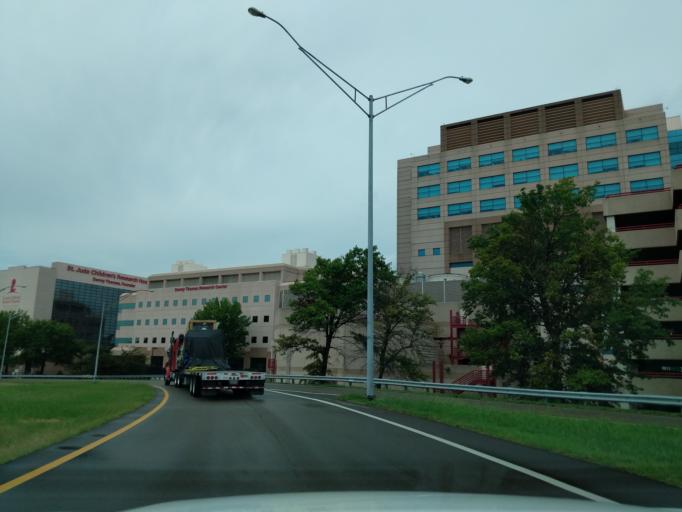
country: US
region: Tennessee
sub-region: Shelby County
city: Memphis
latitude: 35.1525
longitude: -90.0400
